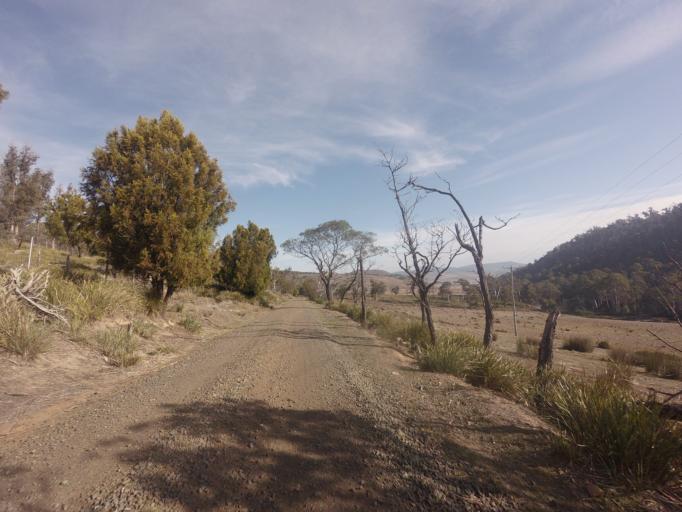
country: AU
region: Tasmania
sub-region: Sorell
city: Sorell
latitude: -42.5341
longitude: 147.4362
